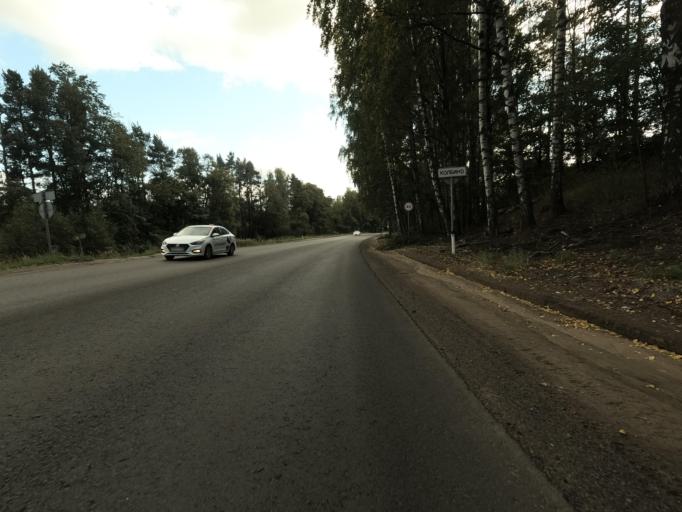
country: RU
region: Leningrad
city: Koltushi
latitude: 59.9469
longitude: 30.6579
